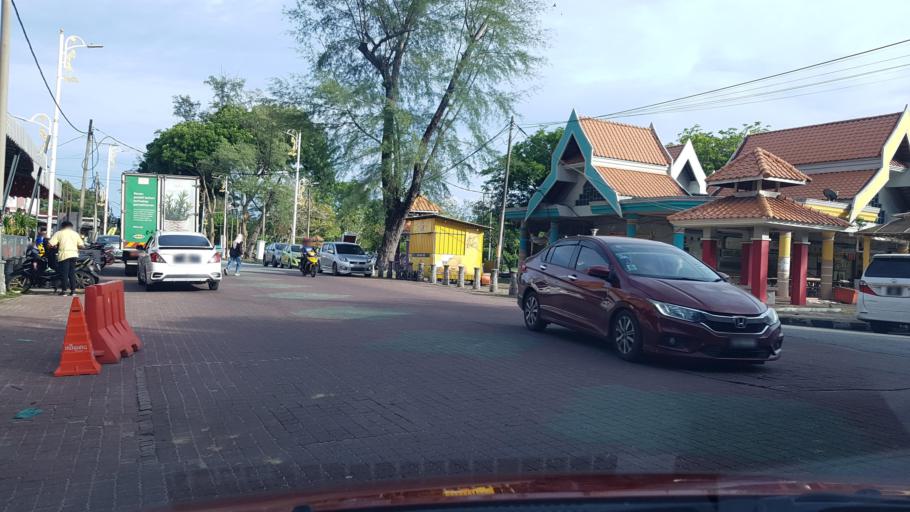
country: MY
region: Terengganu
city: Kuala Terengganu
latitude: 5.3212
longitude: 103.1548
